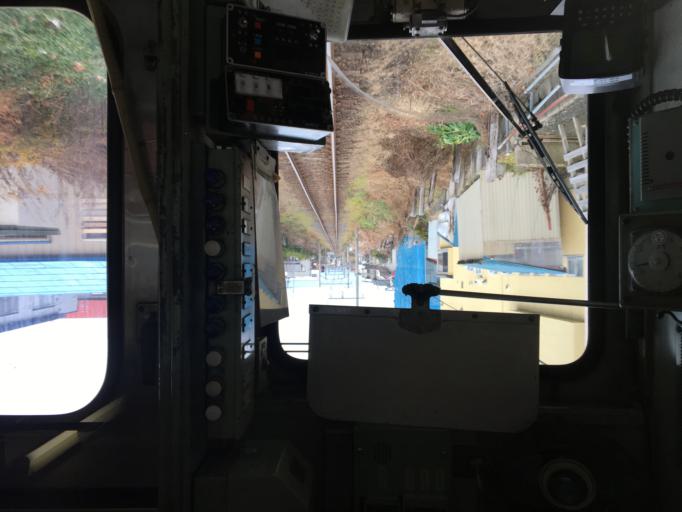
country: JP
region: Aomori
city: Hirosaki
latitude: 40.5806
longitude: 140.4716
